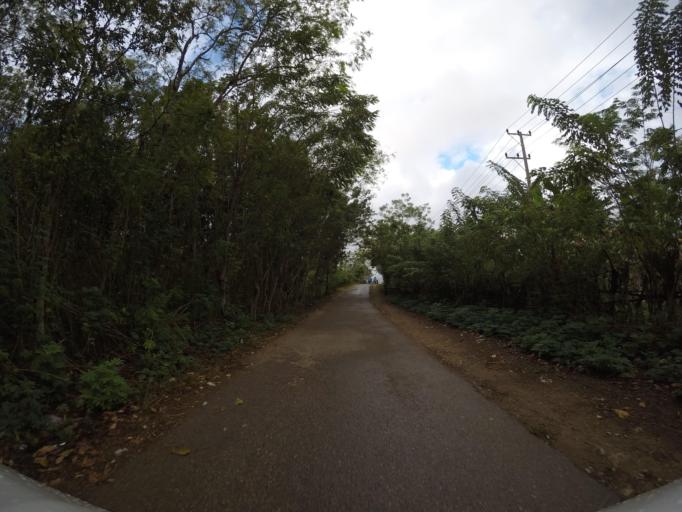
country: TL
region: Lautem
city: Lospalos
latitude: -8.5255
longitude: 126.9880
